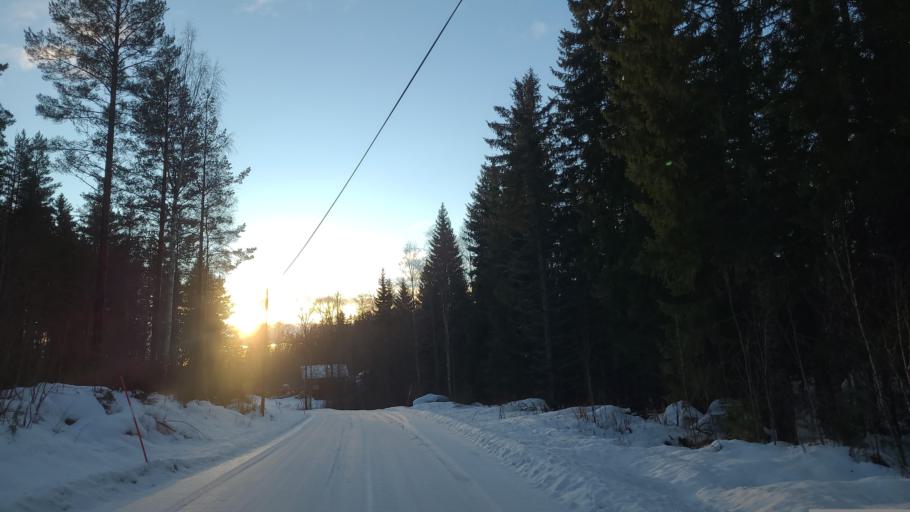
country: SE
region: Gaevleborg
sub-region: Bollnas Kommun
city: Kilafors
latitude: 61.3780
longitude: 16.6827
